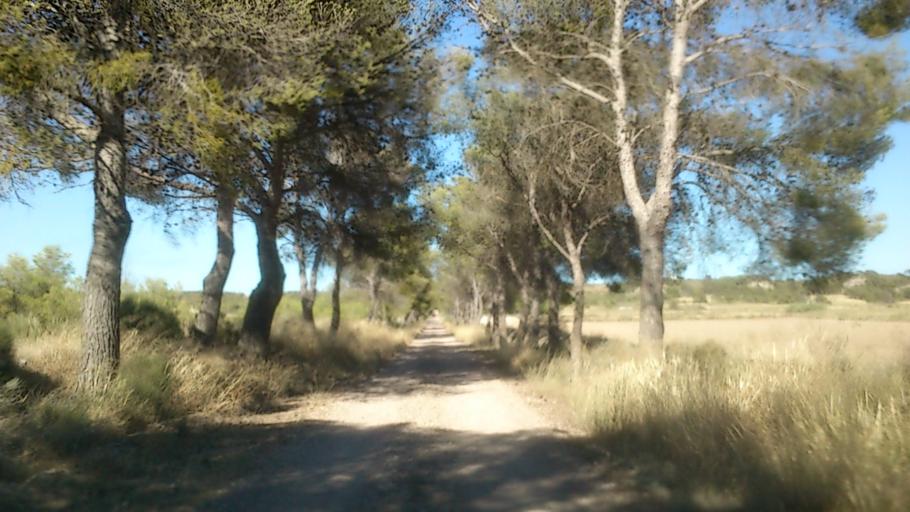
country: ES
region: Aragon
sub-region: Provincia de Zaragoza
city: San Mateo de Gallego
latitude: 41.7711
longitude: -0.7287
